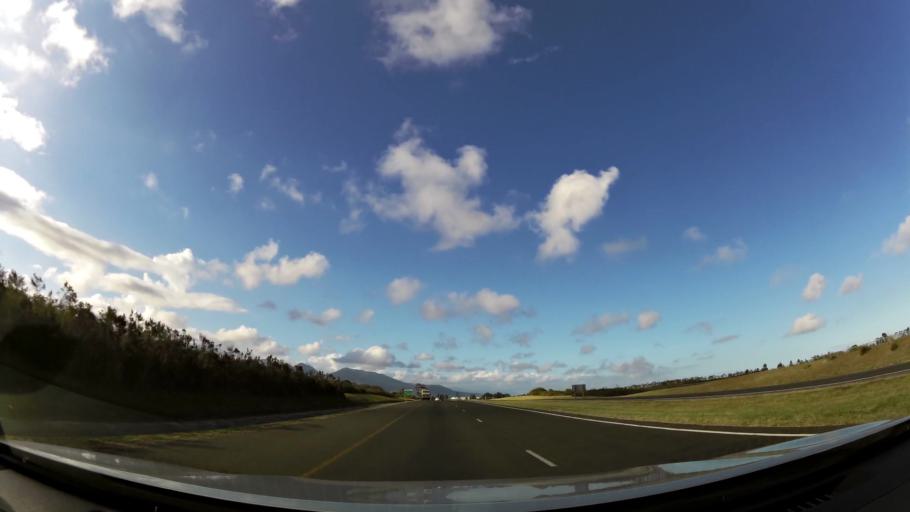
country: ZA
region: Western Cape
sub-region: Eden District Municipality
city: George
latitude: -33.9894
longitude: 22.5022
